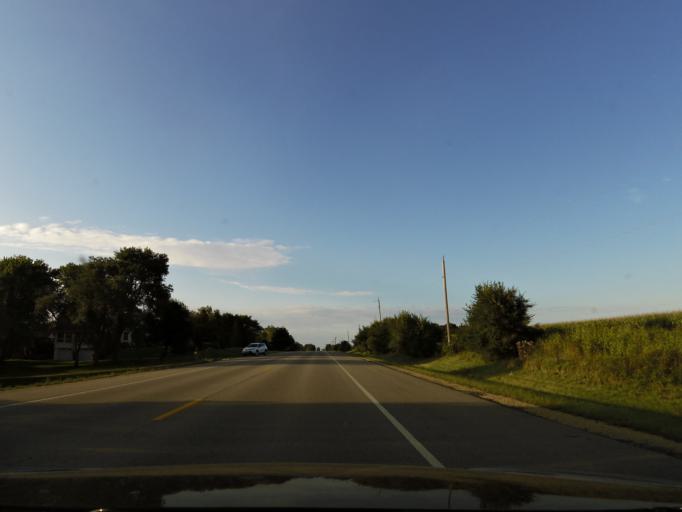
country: US
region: Minnesota
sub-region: Washington County
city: Cottage Grove
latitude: 44.8728
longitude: -92.9032
